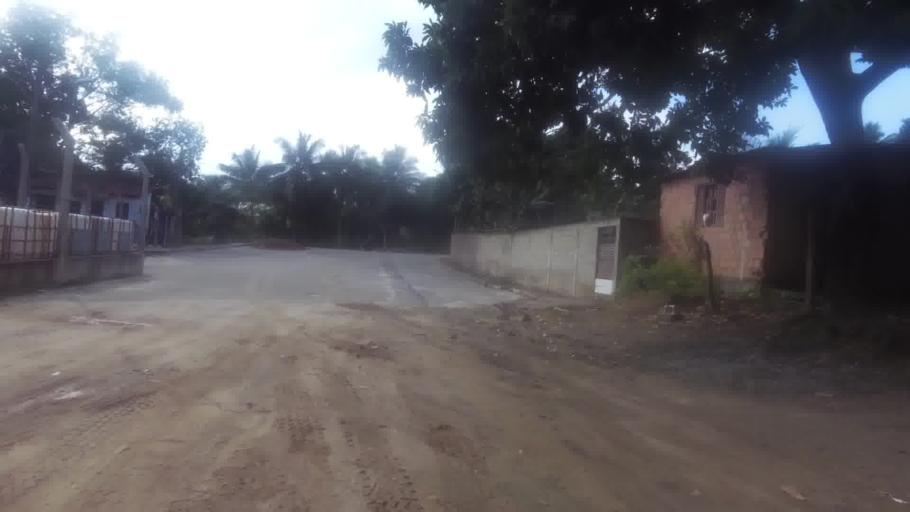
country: BR
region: Espirito Santo
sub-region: Guarapari
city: Guarapari
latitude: -20.7683
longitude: -40.5768
